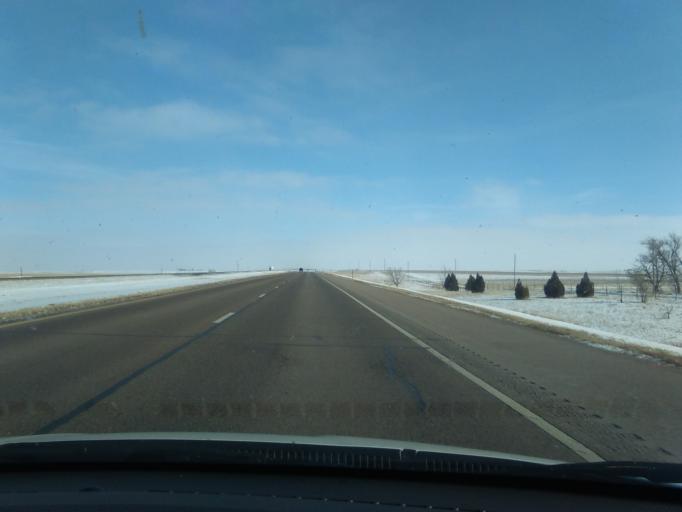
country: US
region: Nebraska
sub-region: Kimball County
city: Kimball
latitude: 41.1919
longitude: -103.8246
